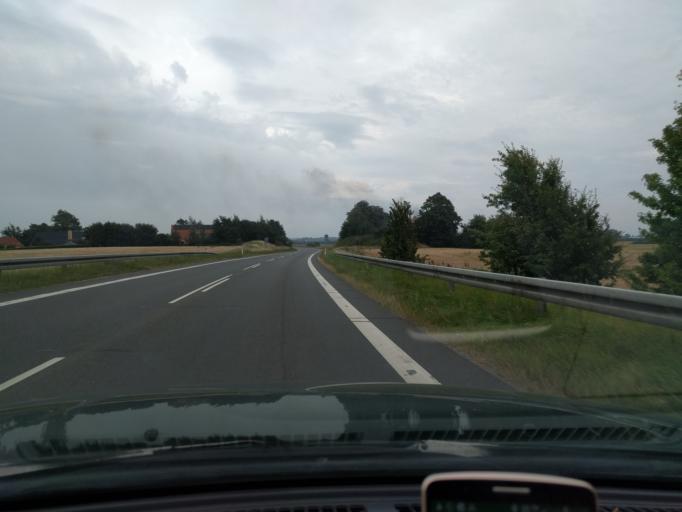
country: DK
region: Zealand
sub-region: Slagelse Kommune
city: Skaelskor
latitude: 55.2473
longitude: 11.3819
